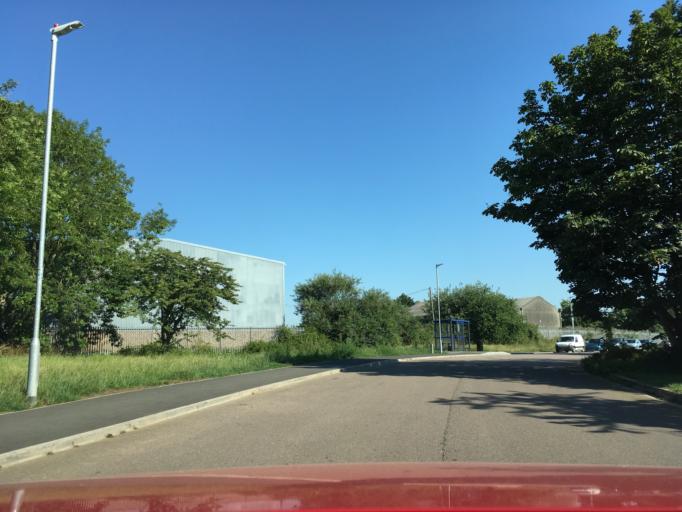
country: GB
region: England
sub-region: South Gloucestershire
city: Pucklechurch
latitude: 51.4813
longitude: -2.4336
